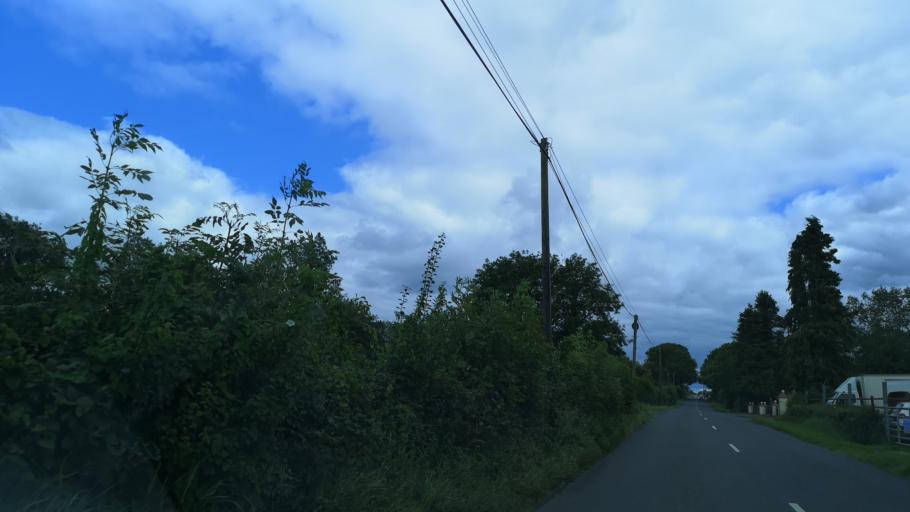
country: IE
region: Leinster
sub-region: Uibh Fhaili
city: Ferbane
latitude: 53.2248
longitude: -7.8702
